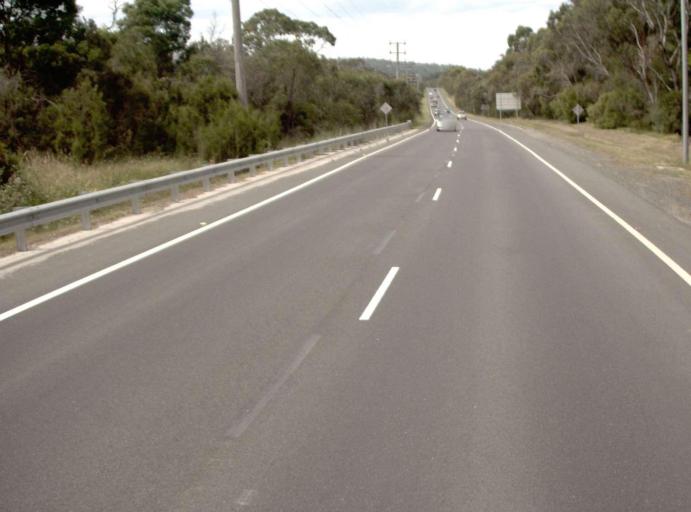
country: AU
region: Victoria
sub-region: Mornington Peninsula
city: Moorooduc
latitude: -38.2239
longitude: 145.1006
